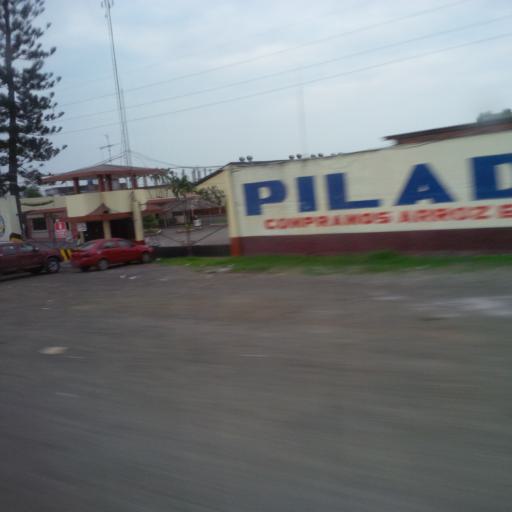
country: EC
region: Canar
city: La Troncal
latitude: -2.3386
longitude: -79.3880
